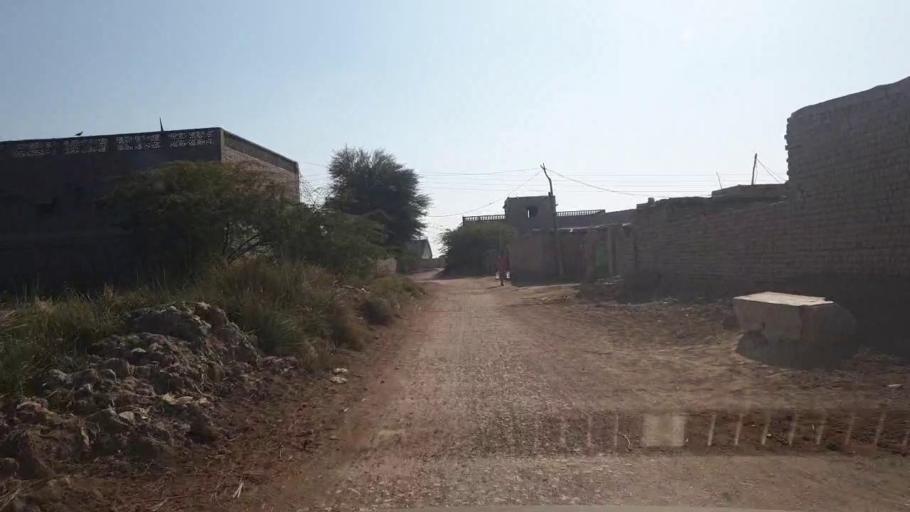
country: PK
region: Sindh
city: Shahpur Chakar
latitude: 26.1468
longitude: 68.6761
